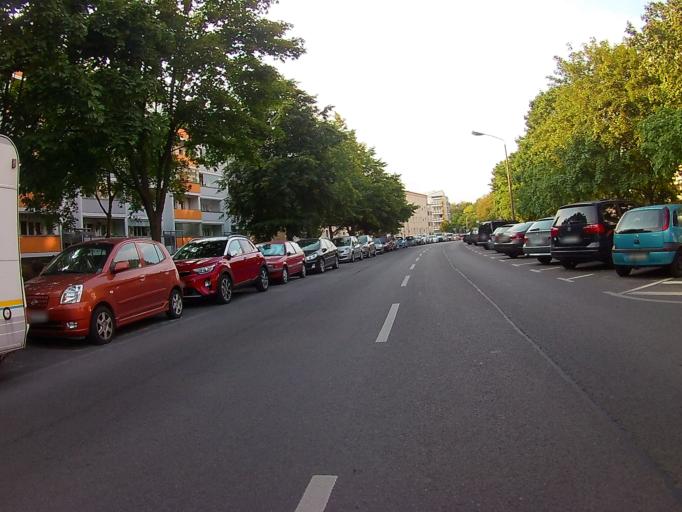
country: DE
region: Berlin
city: Alt-Hohenschoenhausen
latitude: 52.5353
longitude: 13.4996
